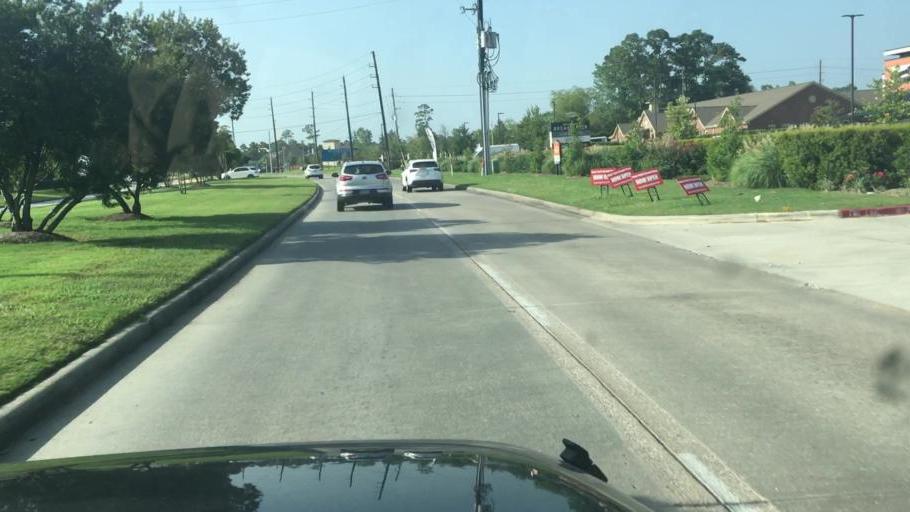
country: US
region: Texas
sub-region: Harris County
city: Atascocita
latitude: 29.9623
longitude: -95.1685
